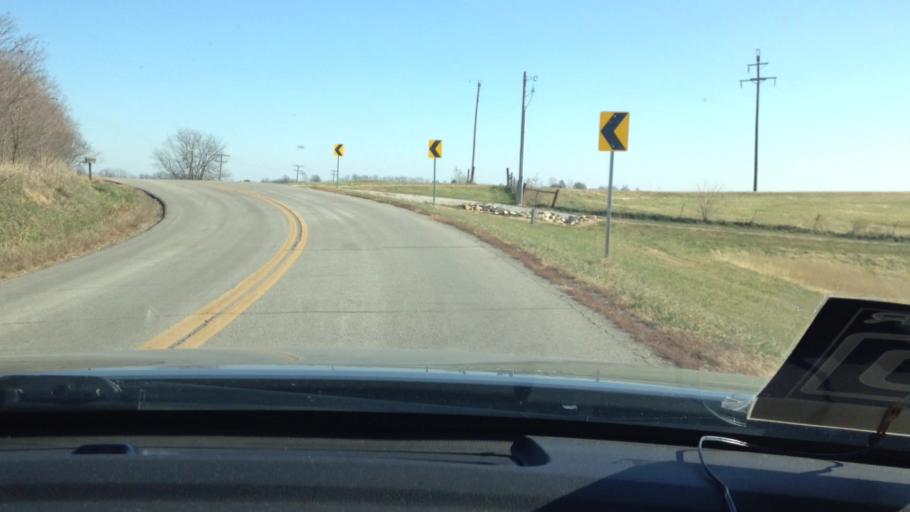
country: US
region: Missouri
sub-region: Platte County
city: Weston
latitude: 39.4828
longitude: -94.8922
